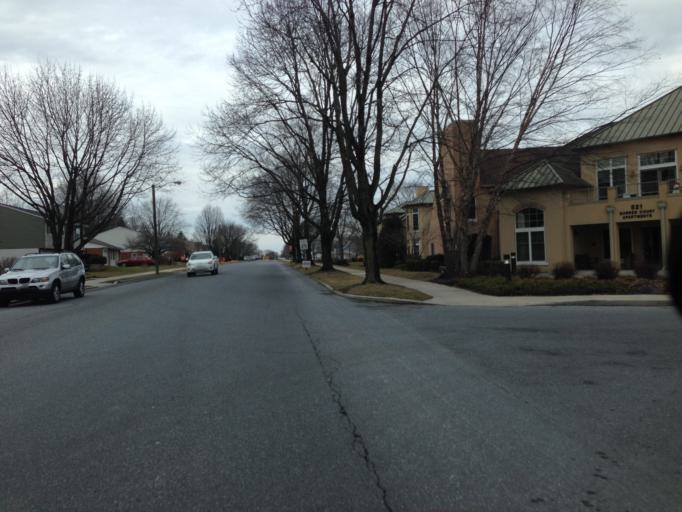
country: US
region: Pennsylvania
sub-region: Lancaster County
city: Lititz
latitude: 40.1513
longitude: -76.3124
